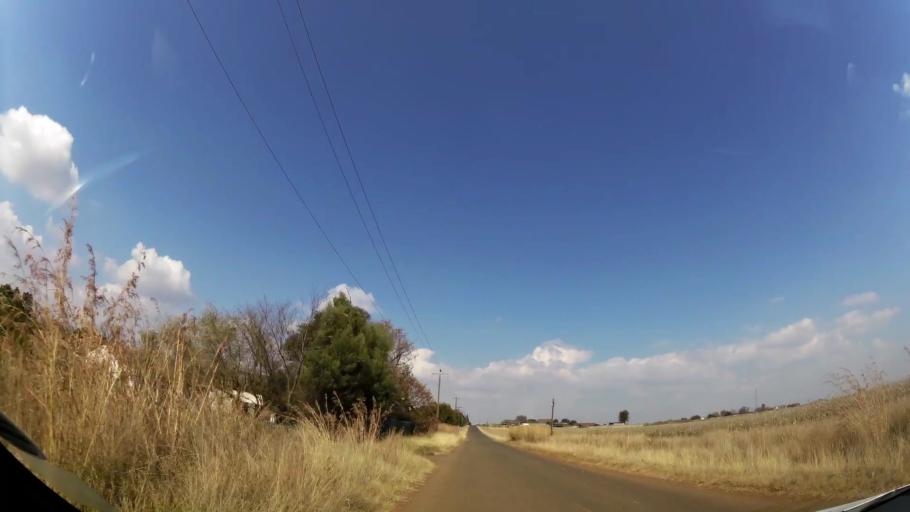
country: ZA
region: Gauteng
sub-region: Ekurhuleni Metropolitan Municipality
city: Springs
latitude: -26.1830
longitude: 28.5336
